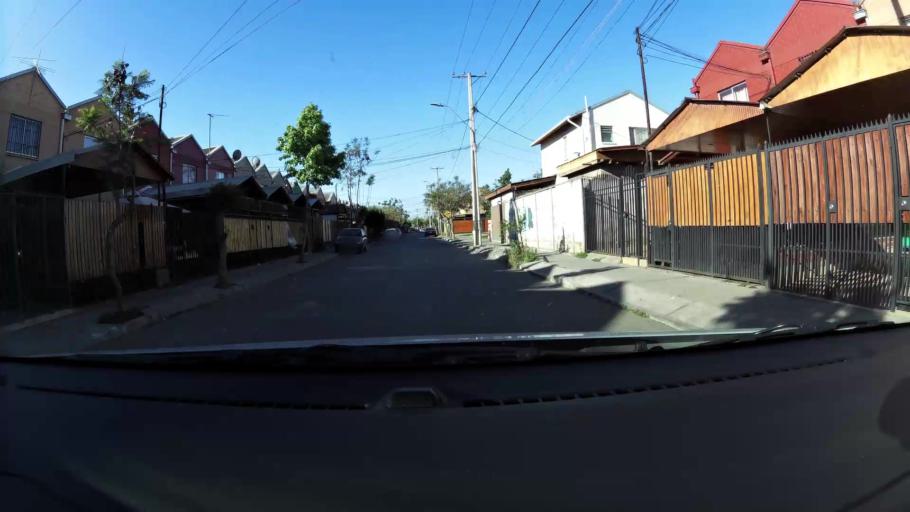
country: CL
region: Santiago Metropolitan
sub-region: Provincia de Maipo
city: San Bernardo
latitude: -33.6029
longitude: -70.6774
